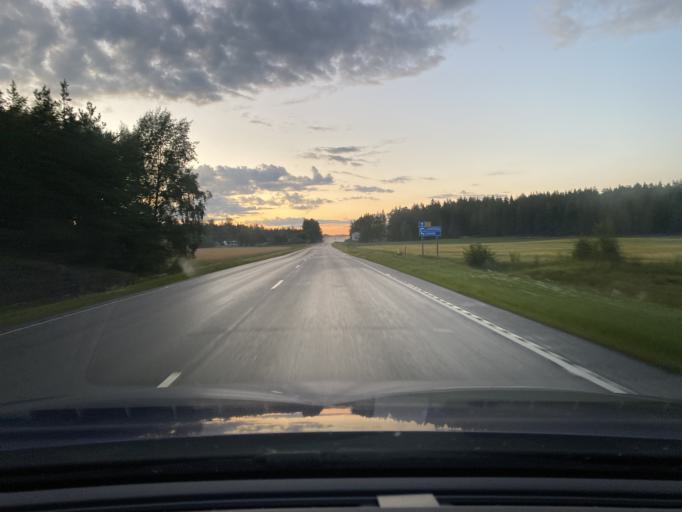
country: FI
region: Varsinais-Suomi
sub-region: Loimaa
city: Aura
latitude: 60.6861
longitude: 22.5636
